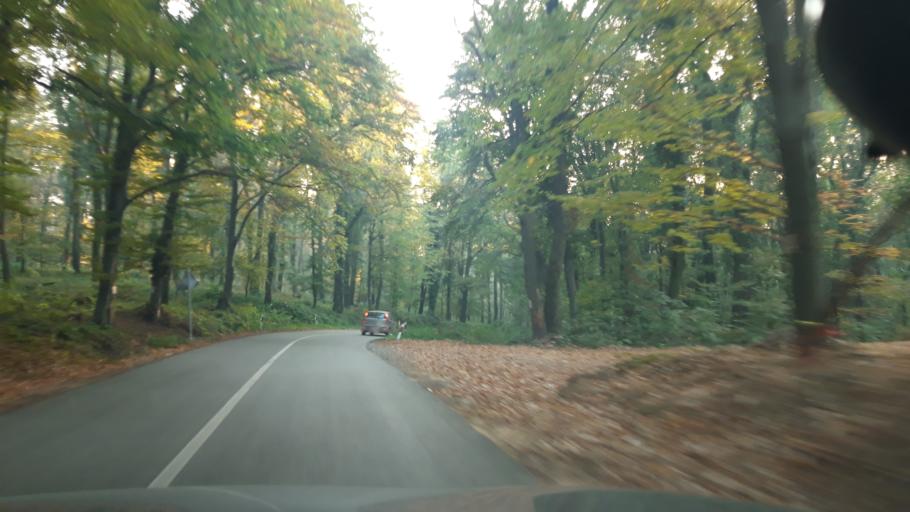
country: RS
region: Autonomna Pokrajina Vojvodina
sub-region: Sremski Okrug
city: Irig
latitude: 45.1559
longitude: 19.8551
